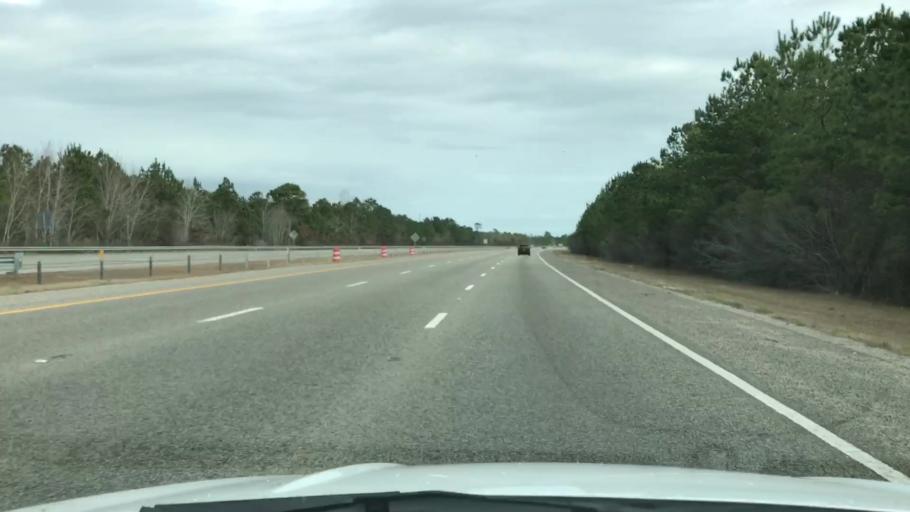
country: US
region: South Carolina
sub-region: Horry County
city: Socastee
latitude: 33.7205
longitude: -78.9969
